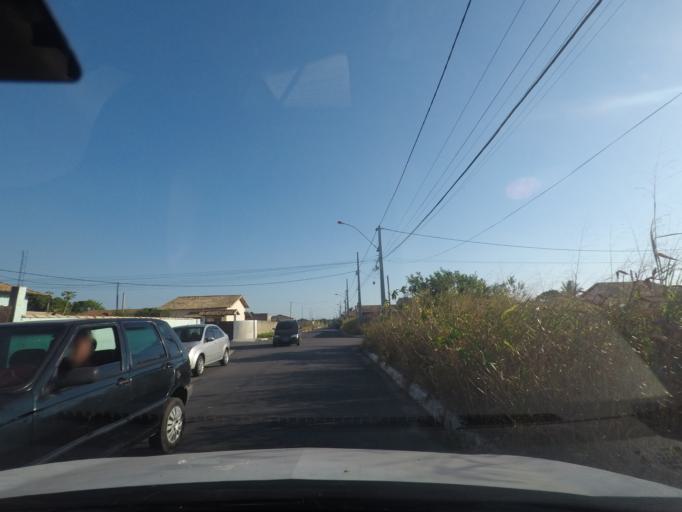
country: BR
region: Rio de Janeiro
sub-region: Marica
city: Marica
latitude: -22.9592
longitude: -42.9379
